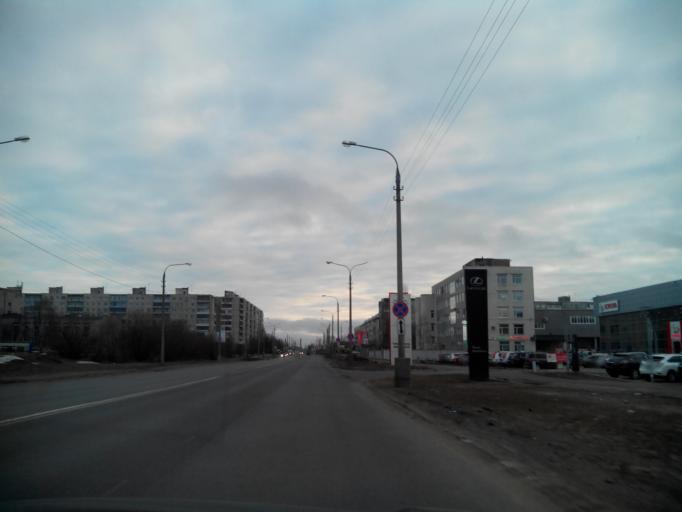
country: RU
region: Arkhangelskaya
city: Arkhangel'sk
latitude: 64.5169
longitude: 40.6749
